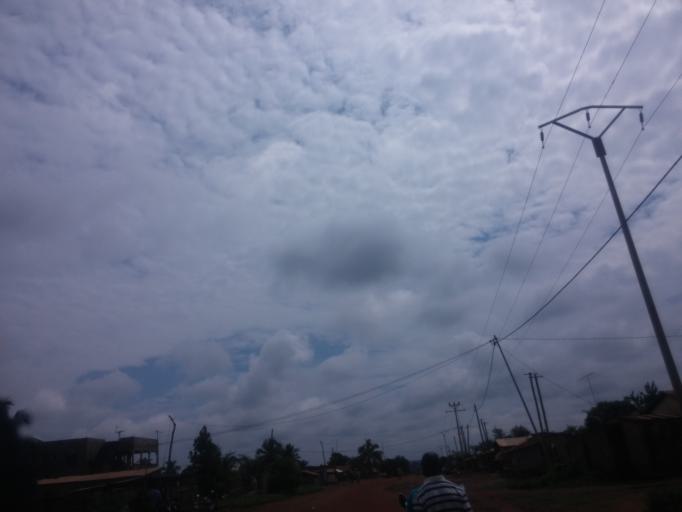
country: TG
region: Centrale
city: Sotouboua
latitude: 8.5545
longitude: 0.9840
